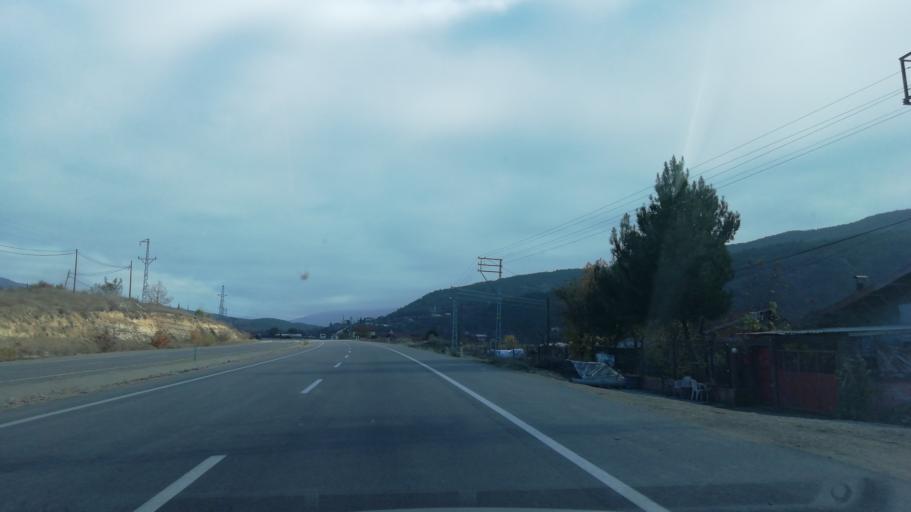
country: TR
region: Karabuk
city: Safranbolu
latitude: 41.2163
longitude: 32.7524
